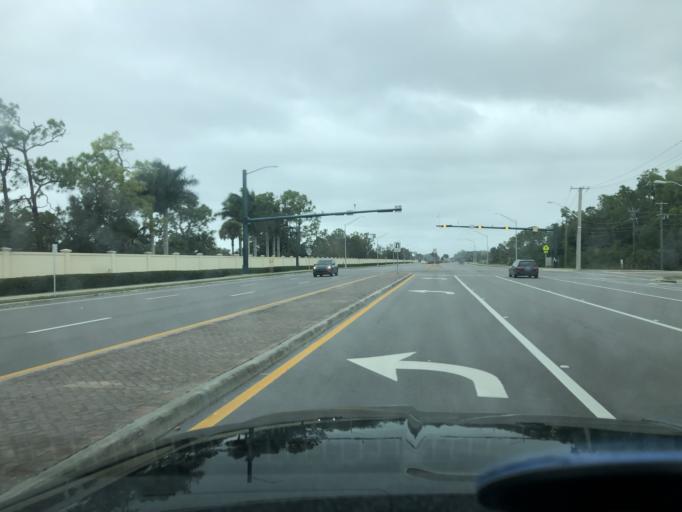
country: US
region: Florida
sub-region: Collier County
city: Lely
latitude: 26.1457
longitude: -81.7185
